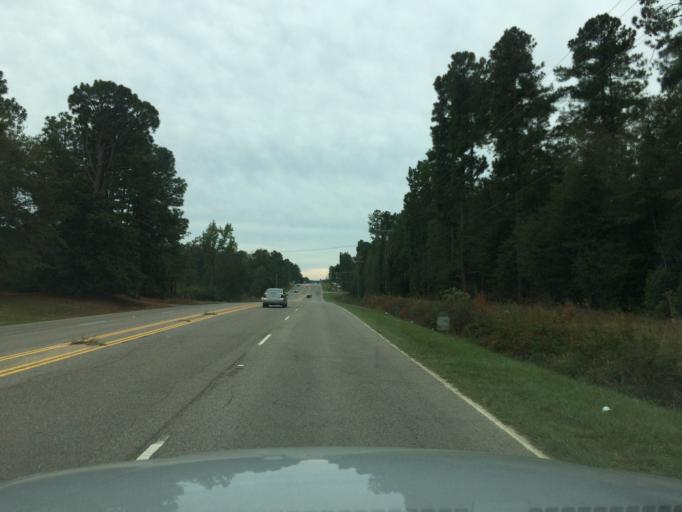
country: US
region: South Carolina
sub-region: Aiken County
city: New Ellenton
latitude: 33.4394
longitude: -81.6864
